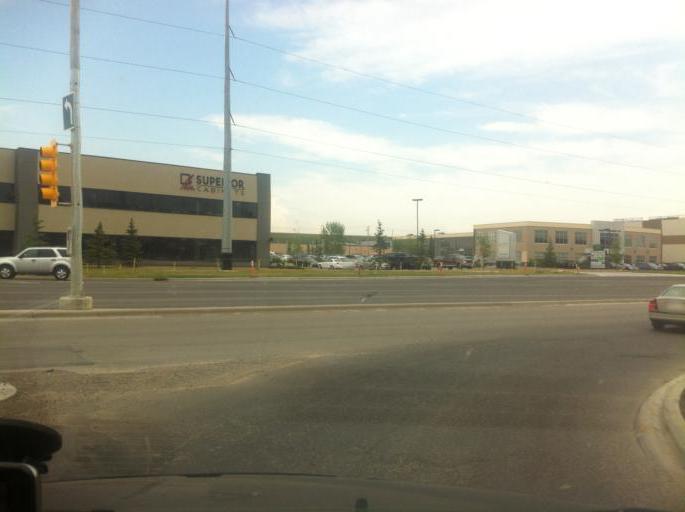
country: CA
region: Alberta
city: Calgary
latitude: 50.9563
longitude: -114.0016
